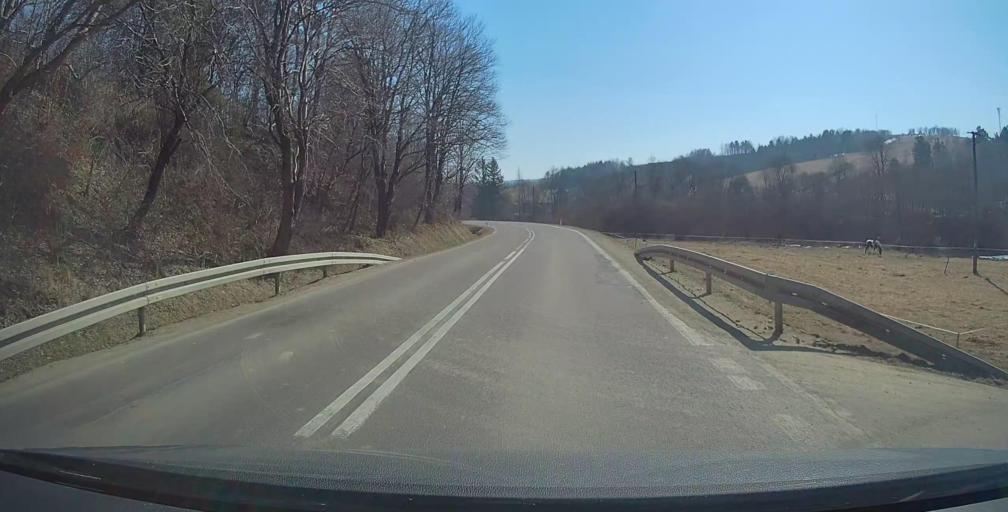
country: PL
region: Subcarpathian Voivodeship
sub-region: Powiat bieszczadzki
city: Ustrzyki Dolne
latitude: 49.5673
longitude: 22.5554
